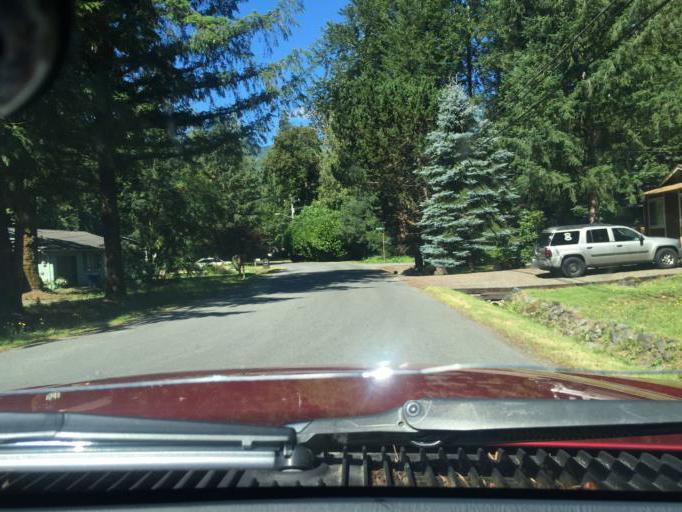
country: US
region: Washington
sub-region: King County
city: Riverbend
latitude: 47.4681
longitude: -121.7485
